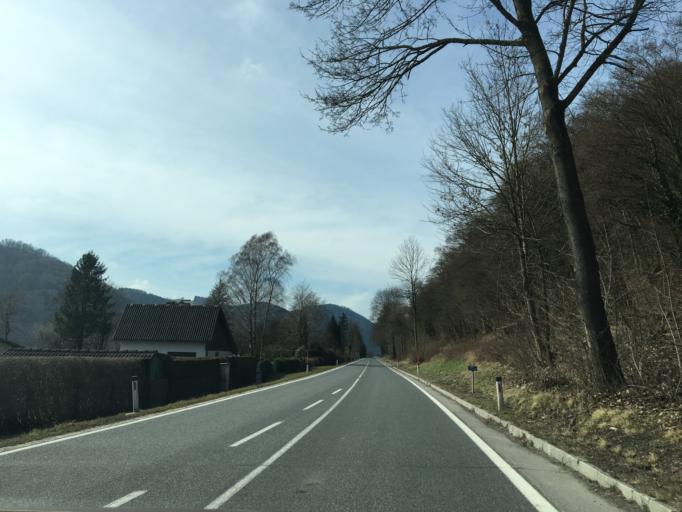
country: AT
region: Lower Austria
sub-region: Politischer Bezirk Melk
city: Nochling
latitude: 48.1970
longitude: 14.9970
